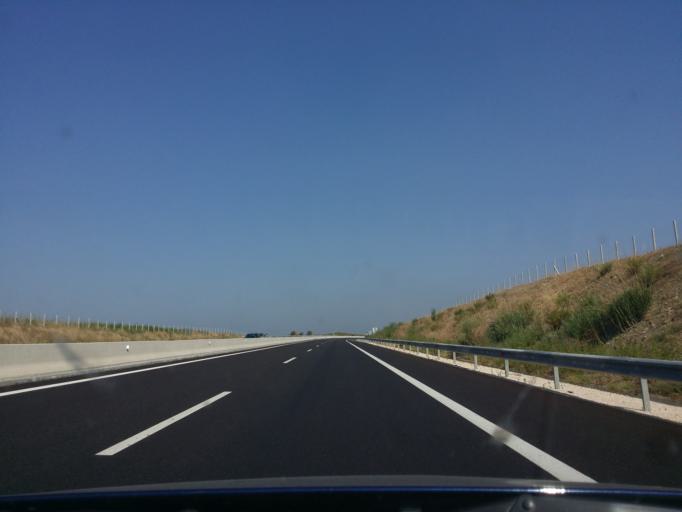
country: GR
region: West Greece
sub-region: Nomos Aitolias kai Akarnanias
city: Menidi
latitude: 39.0201
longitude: 21.1488
